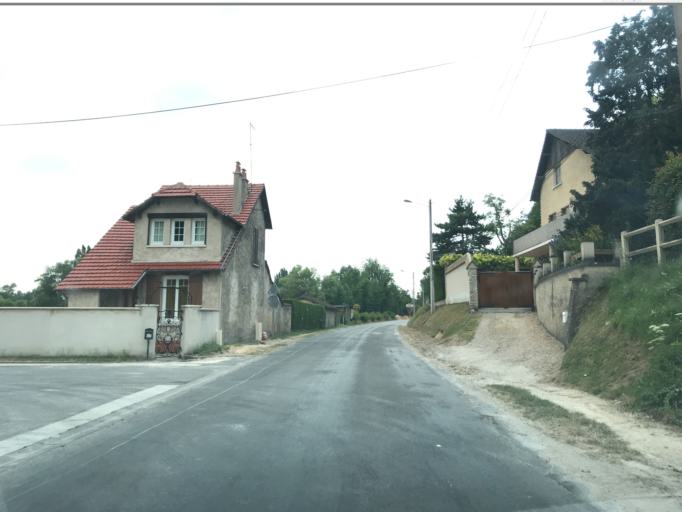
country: FR
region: Haute-Normandie
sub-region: Departement de l'Eure
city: Ivry-la-Bataille
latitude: 48.8767
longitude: 1.4573
